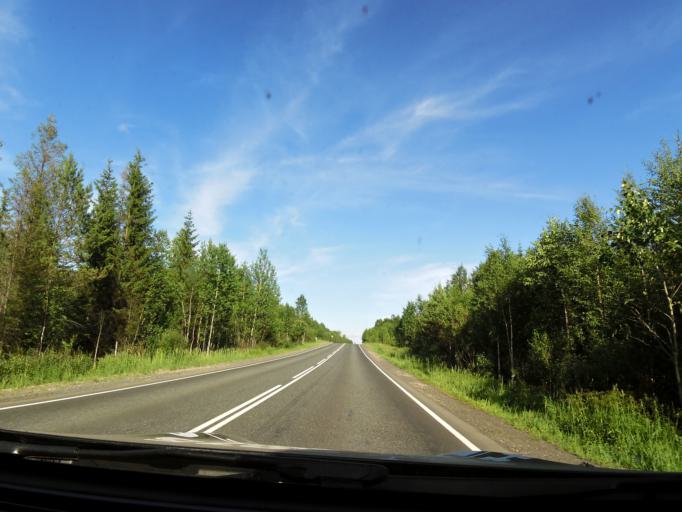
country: RU
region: Kirov
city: Chernaya Kholunitsa
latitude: 58.8738
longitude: 51.5029
